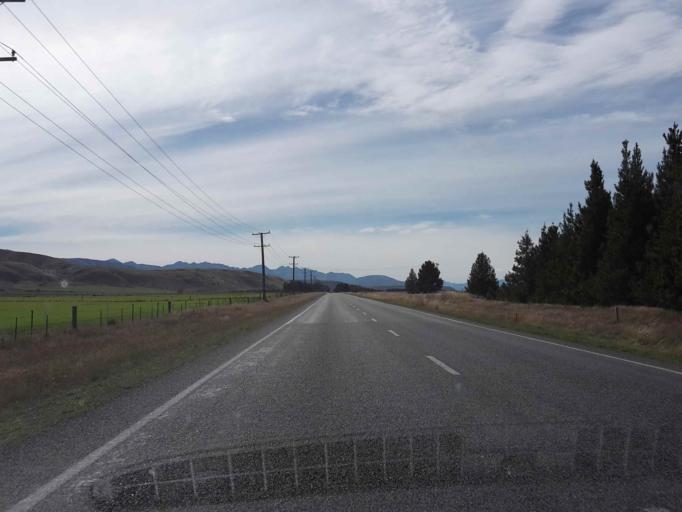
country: NZ
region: Otago
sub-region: Queenstown-Lakes District
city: Wanaka
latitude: -44.4009
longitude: 169.9937
